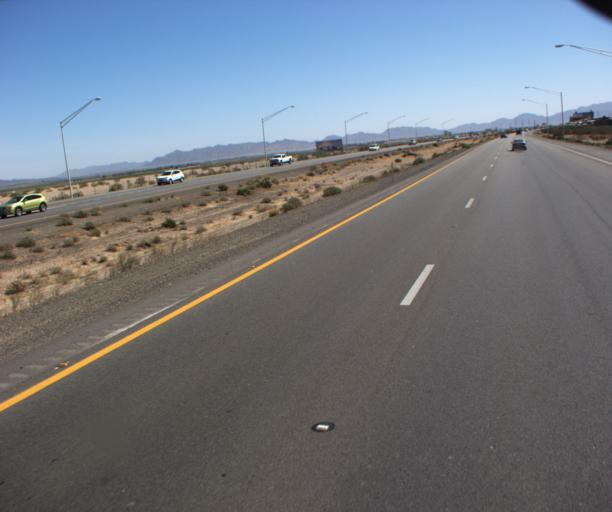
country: US
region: Arizona
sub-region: Yuma County
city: Yuma
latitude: 32.6878
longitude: -114.5759
